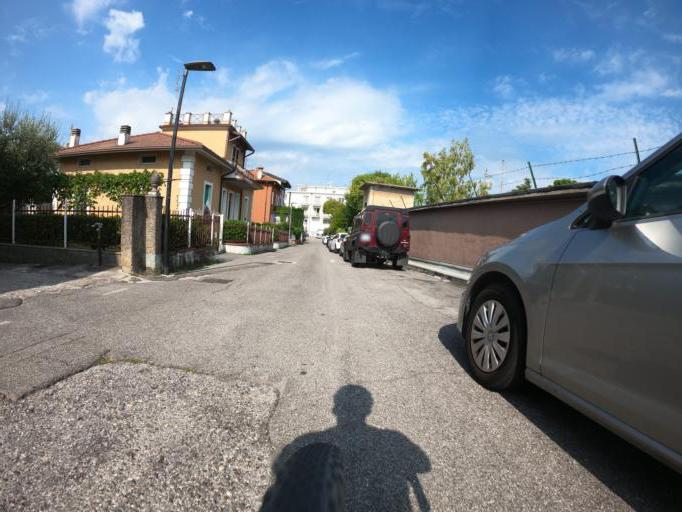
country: IT
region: Lombardy
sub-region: Provincia di Brescia
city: Desenzano del Garda
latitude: 45.4661
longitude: 10.5422
